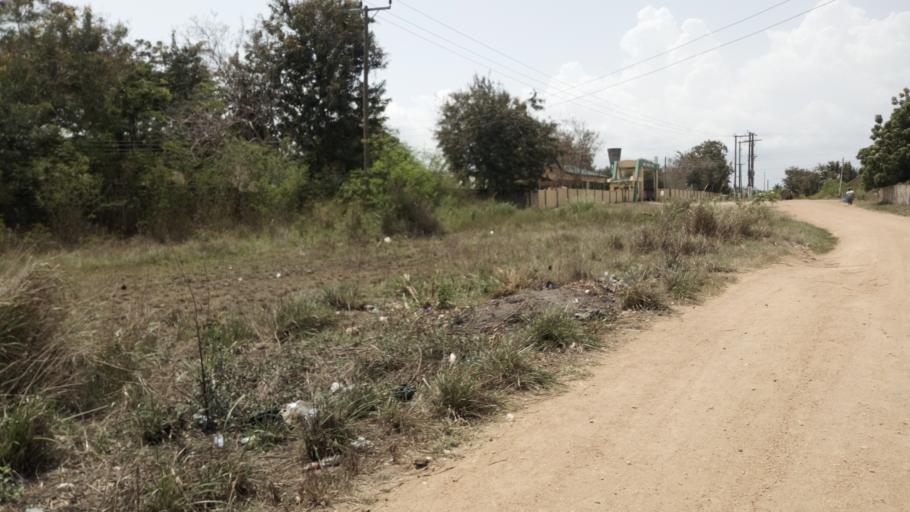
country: GH
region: Central
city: Winneba
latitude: 5.3559
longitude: -0.6359
